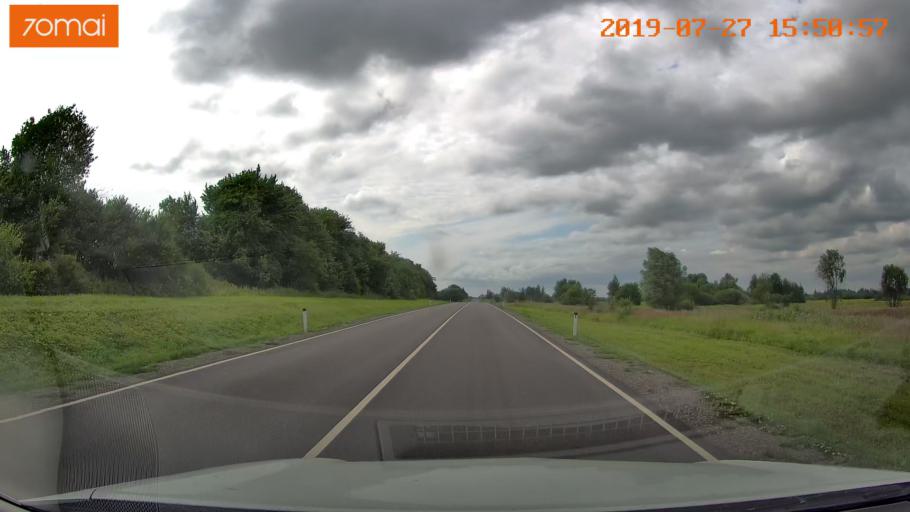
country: RU
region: Kaliningrad
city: Chernyakhovsk
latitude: 54.6019
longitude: 21.9932
